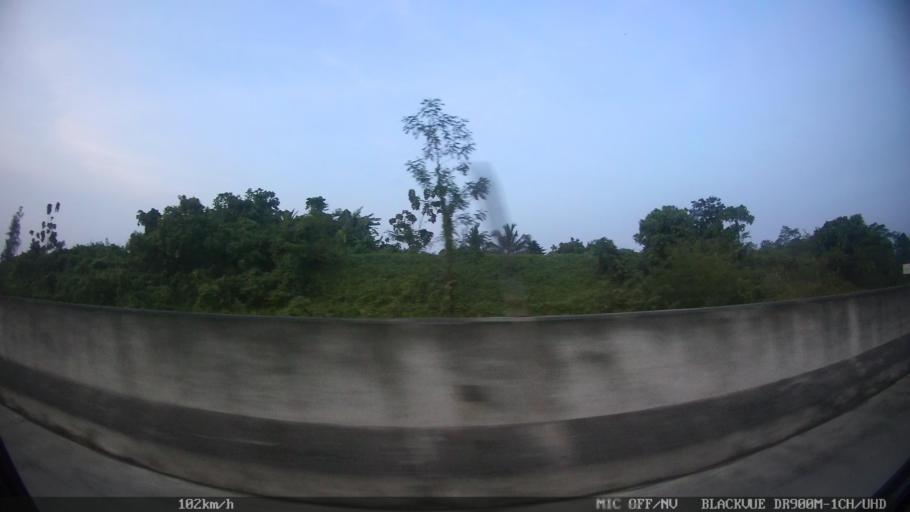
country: ID
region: Lampung
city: Pasuruan
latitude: -5.7045
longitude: 105.6382
